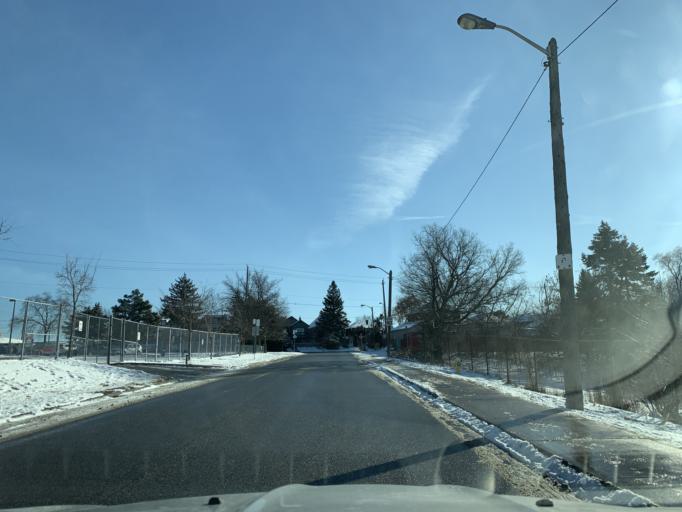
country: CA
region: Ontario
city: Toronto
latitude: 43.6812
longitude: -79.4783
